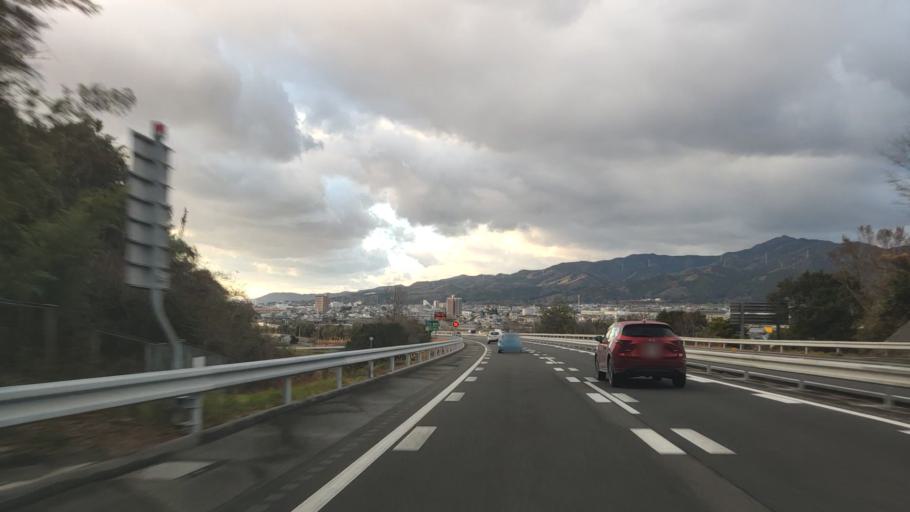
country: JP
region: Ehime
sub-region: Shikoku-chuo Shi
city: Matsuyama
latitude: 33.7927
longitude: 132.9129
